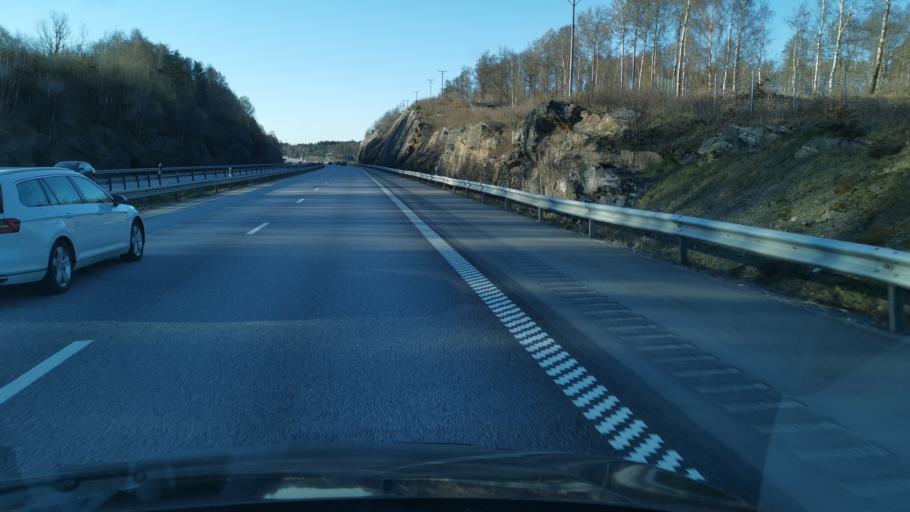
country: SE
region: Vaestra Goetaland
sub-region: Kungalvs Kommun
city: Kode
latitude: 57.9294
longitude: 11.8746
